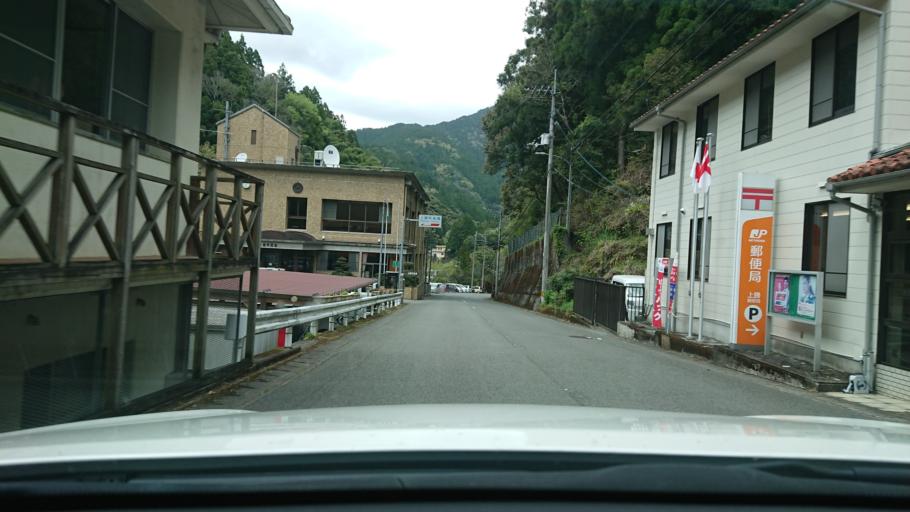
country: JP
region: Tokushima
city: Ishii
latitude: 33.8885
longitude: 134.4022
